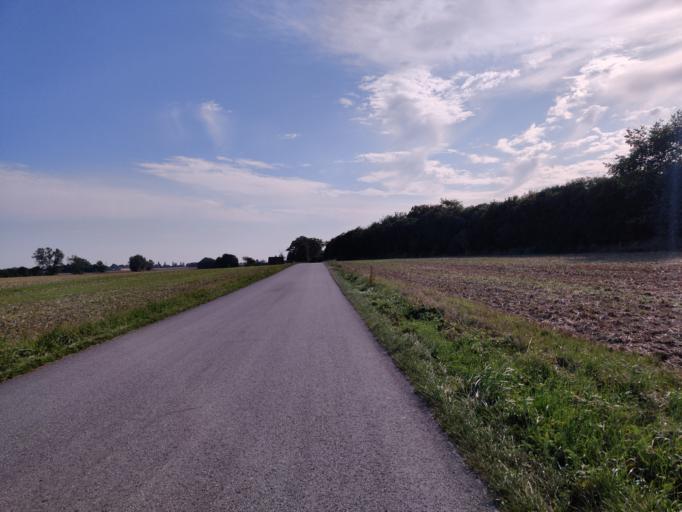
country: DK
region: Zealand
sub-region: Guldborgsund Kommune
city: Nykobing Falster
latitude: 54.6943
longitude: 11.9035
